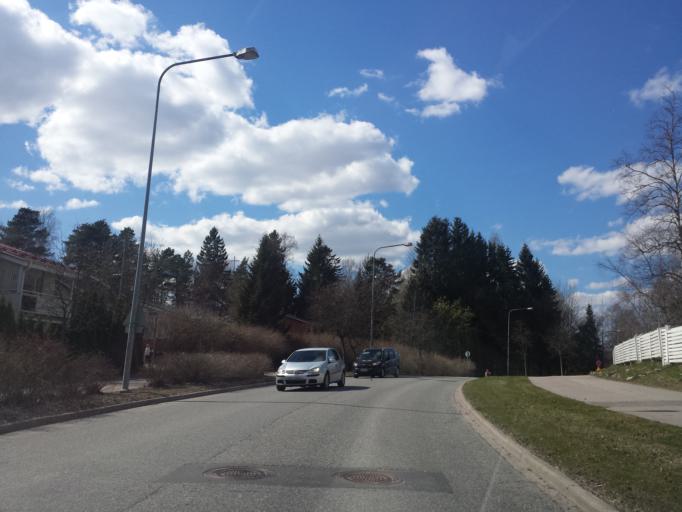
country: FI
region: Uusimaa
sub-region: Helsinki
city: Vantaa
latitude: 60.2700
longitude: 25.0562
